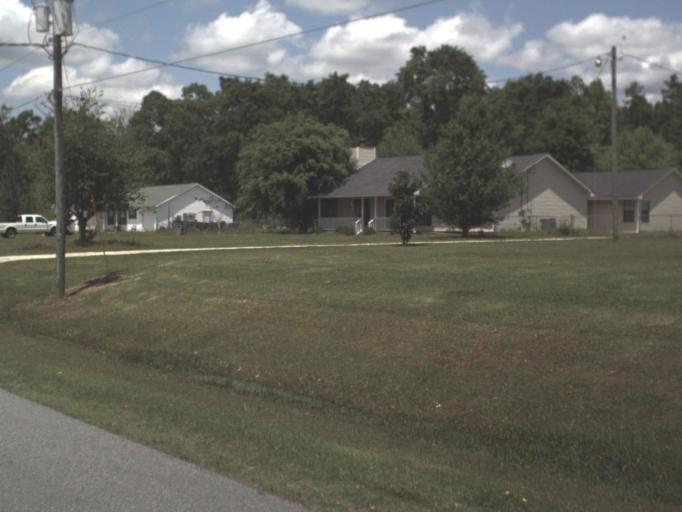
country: US
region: Florida
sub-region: Escambia County
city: Molino
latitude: 30.7287
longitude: -87.3461
